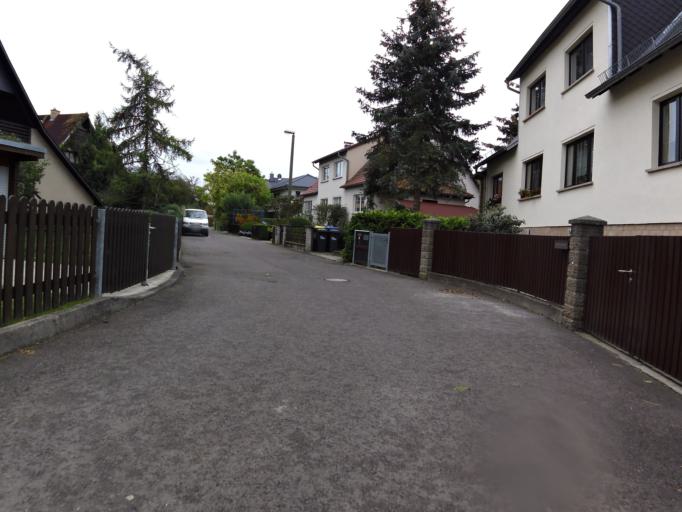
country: DE
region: Saxony
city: Markkleeberg
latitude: 51.2915
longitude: 12.3608
